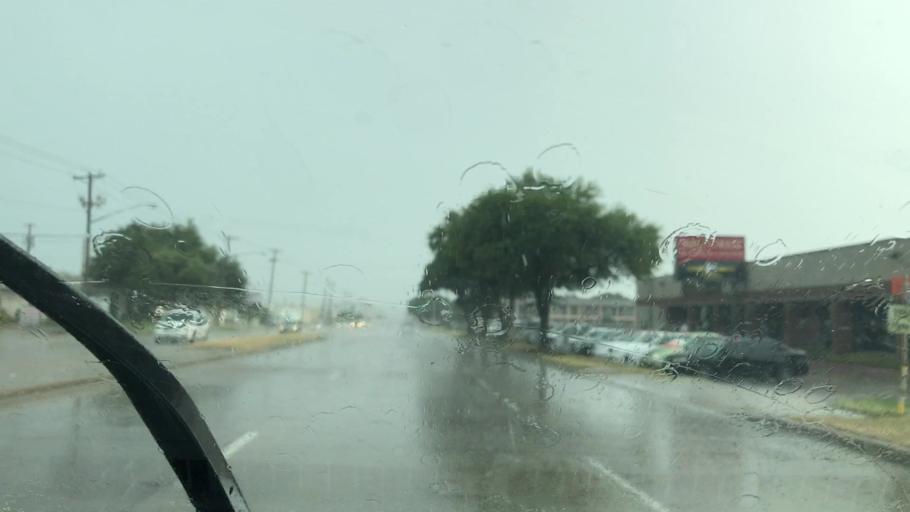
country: US
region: Texas
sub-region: Dallas County
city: Richardson
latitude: 32.9064
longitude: -96.7006
